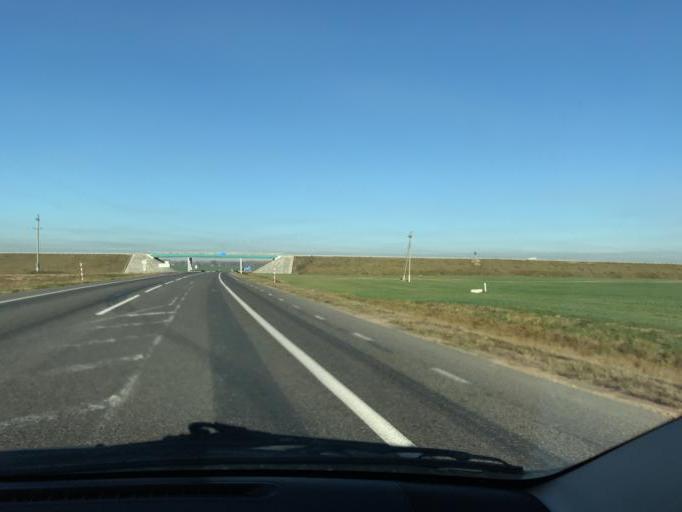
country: BY
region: Vitebsk
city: Vitebsk
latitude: 55.1087
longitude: 30.1078
